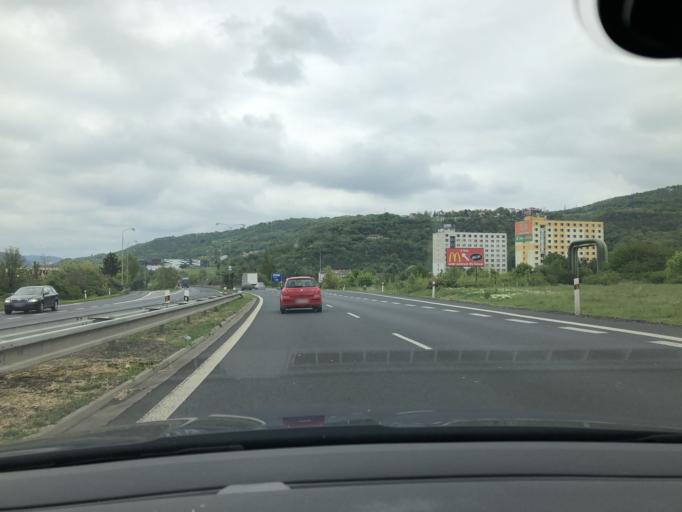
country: CZ
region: Ustecky
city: Trmice
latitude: 50.6477
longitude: 14.0000
